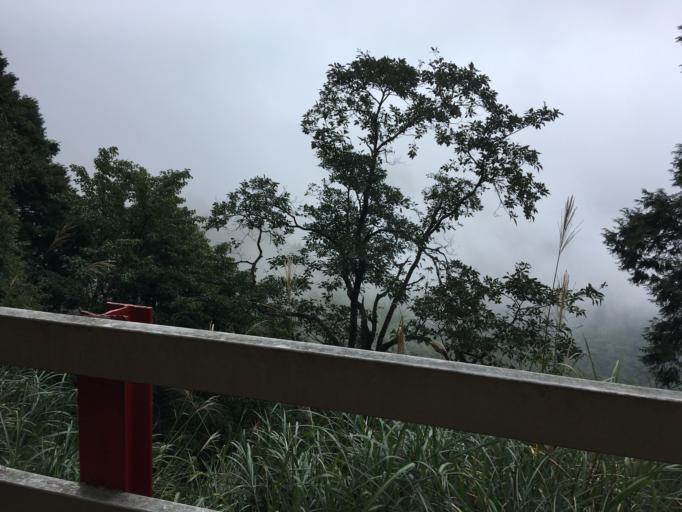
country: TW
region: Taiwan
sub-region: Yilan
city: Yilan
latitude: 24.4845
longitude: 121.5350
